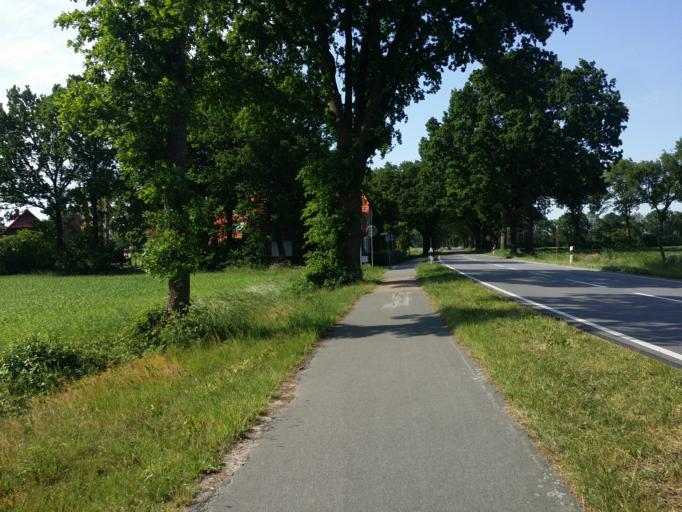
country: DE
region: Lower Saxony
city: Wiefelstede
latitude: 53.2637
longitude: 8.1118
